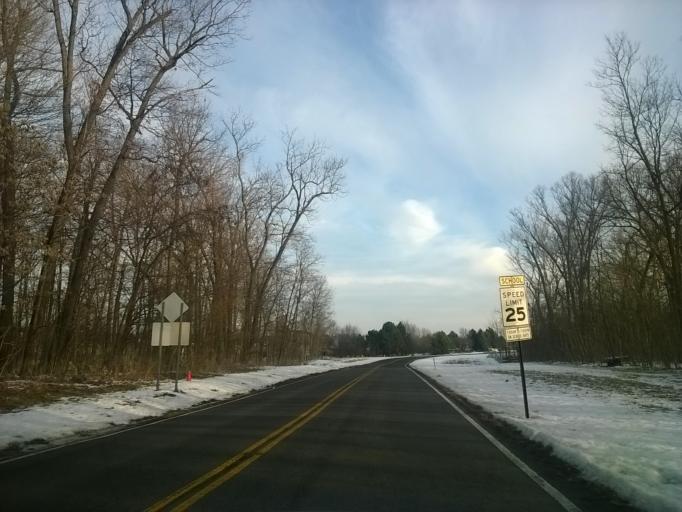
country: US
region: Indiana
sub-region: Hamilton County
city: Fishers
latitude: 39.9858
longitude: -86.0481
